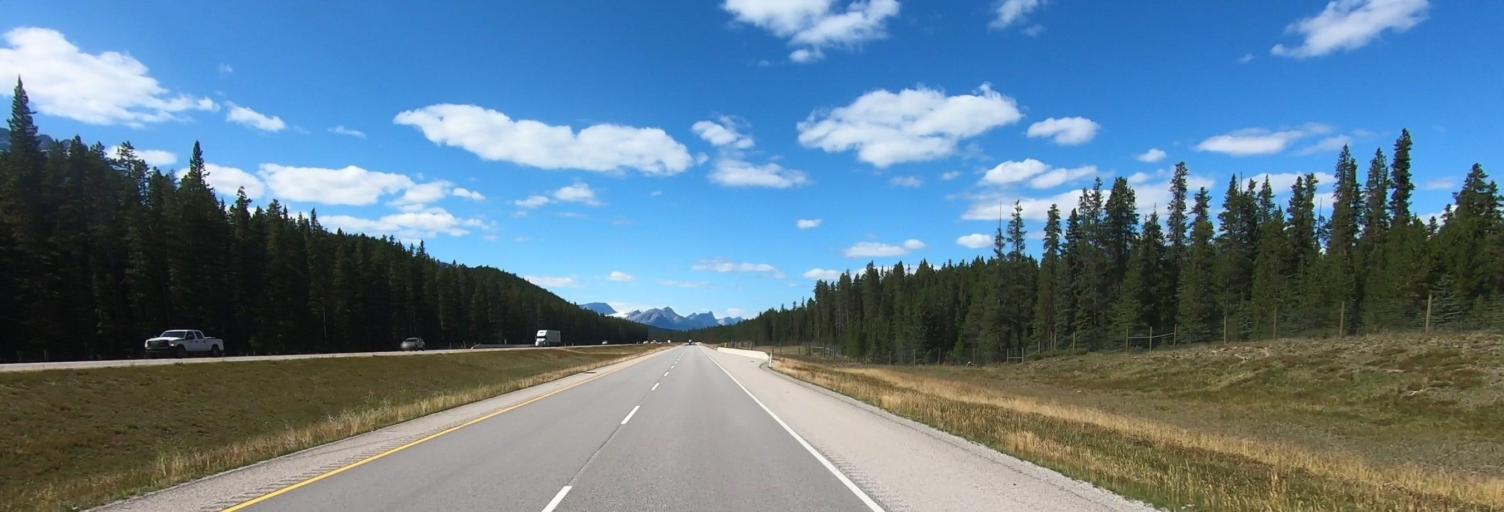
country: CA
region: Alberta
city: Lake Louise
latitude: 51.3387
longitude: -116.0636
